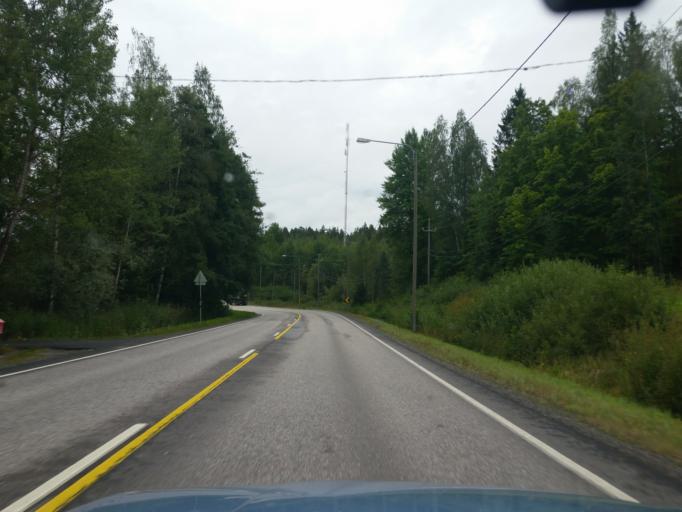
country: FI
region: Uusimaa
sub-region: Helsinki
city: Vihti
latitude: 60.3370
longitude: 24.1986
